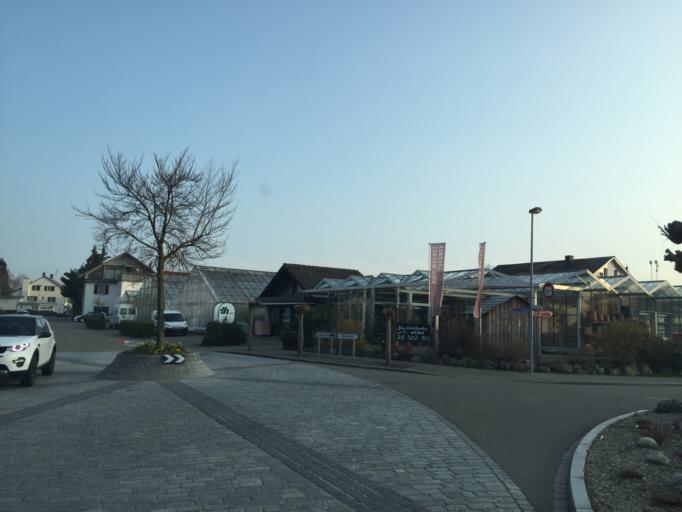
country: CH
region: Zurich
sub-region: Bezirk Andelfingen
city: Dachsen
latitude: 47.6679
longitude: 8.6146
